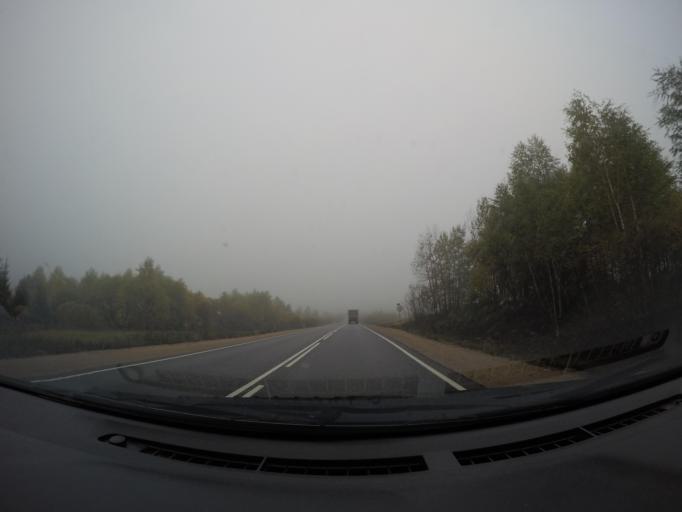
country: RU
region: Moskovskaya
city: Novopetrovskoye
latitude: 55.8380
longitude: 36.4559
